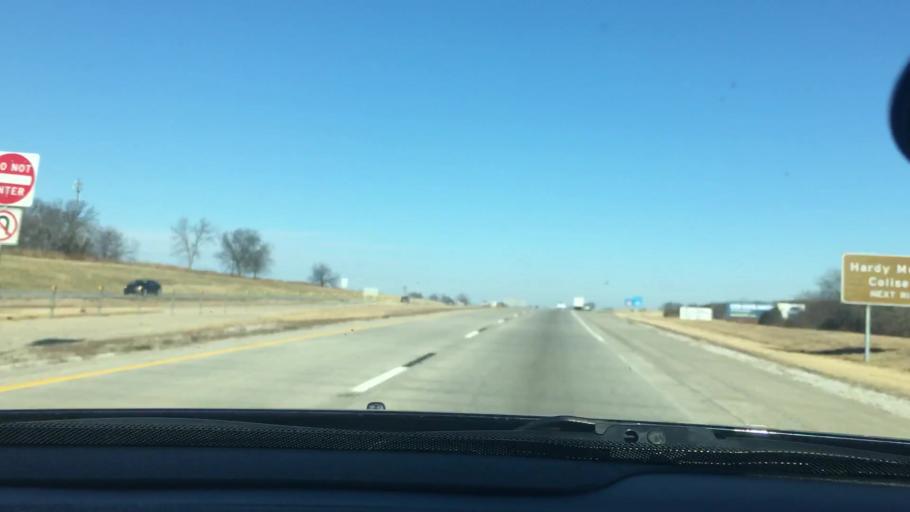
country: US
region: Oklahoma
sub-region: Carter County
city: Ardmore
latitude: 34.1242
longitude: -97.1558
